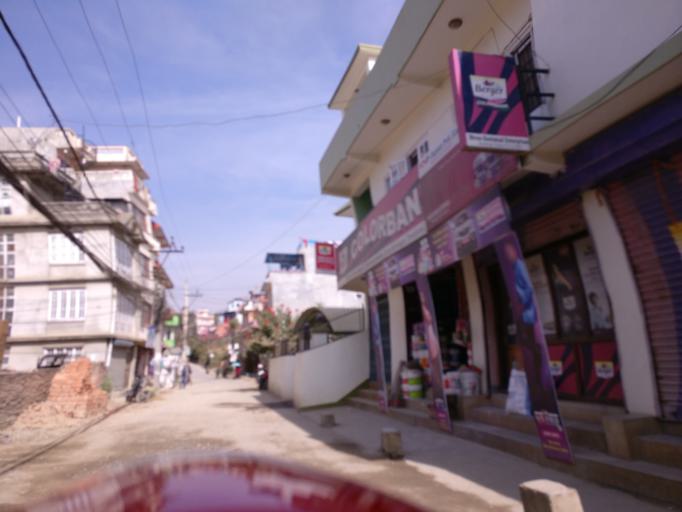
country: NP
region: Central Region
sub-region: Bagmati Zone
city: Patan
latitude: 27.6597
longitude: 85.3140
